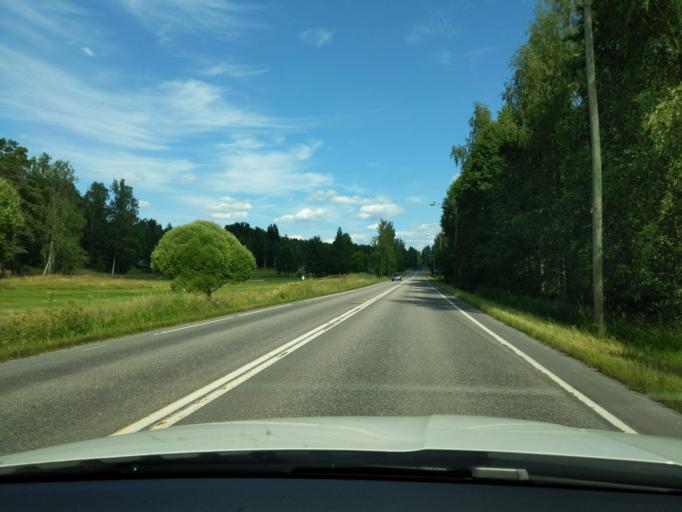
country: FI
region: Paijanne Tavastia
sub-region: Lahti
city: Lahti
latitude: 61.0231
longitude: 25.7241
